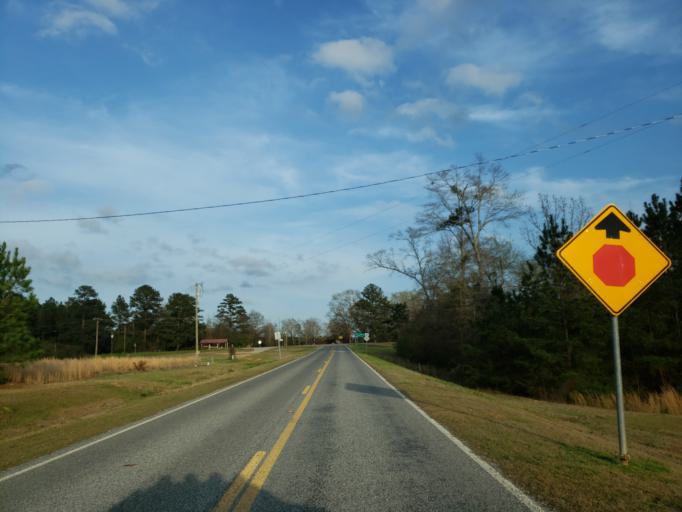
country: US
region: Mississippi
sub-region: Clarke County
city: Stonewall
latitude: 32.1734
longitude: -88.6809
